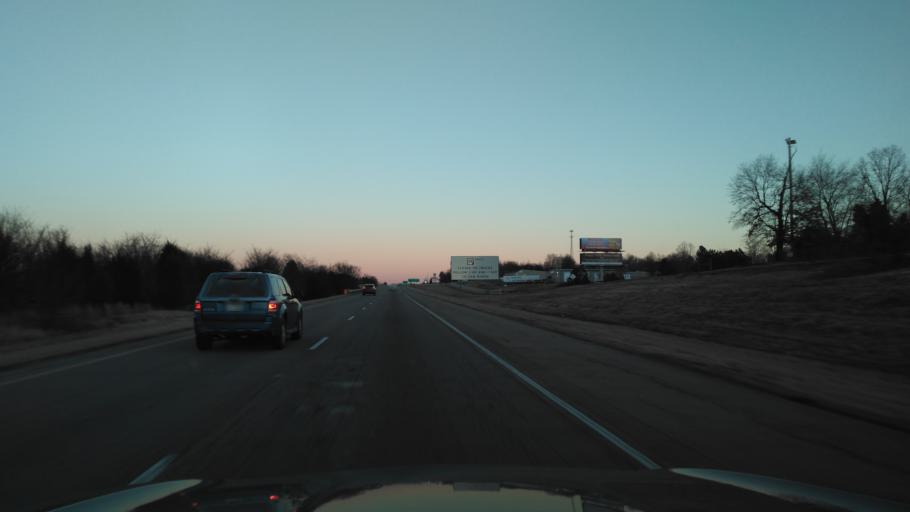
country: US
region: Arkansas
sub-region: Crawford County
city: Van Buren
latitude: 35.4645
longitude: -94.3707
